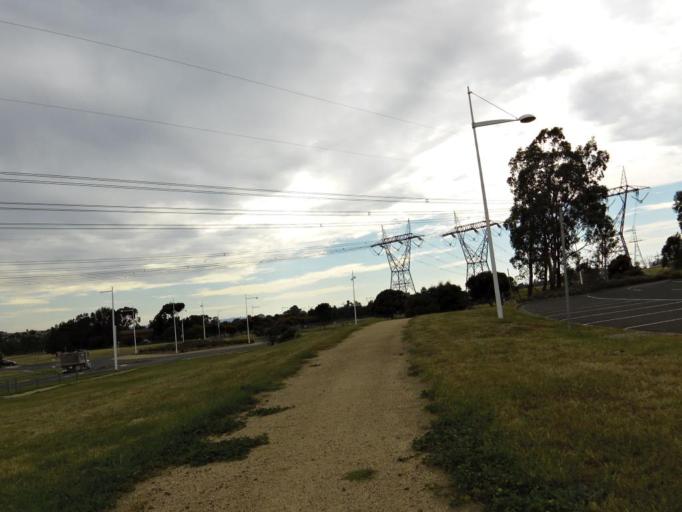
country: AU
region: Victoria
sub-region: Whittlesea
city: Mill Park
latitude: -37.6428
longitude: 145.0682
